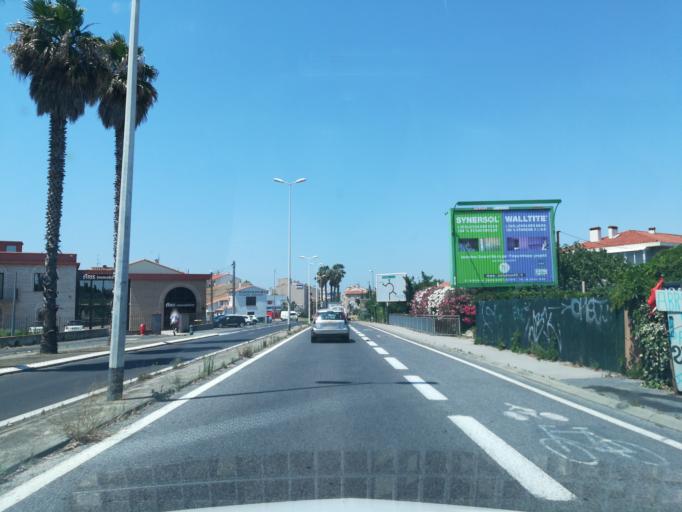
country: FR
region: Languedoc-Roussillon
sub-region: Departement des Pyrenees-Orientales
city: Perpignan
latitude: 42.6873
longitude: 2.8956
